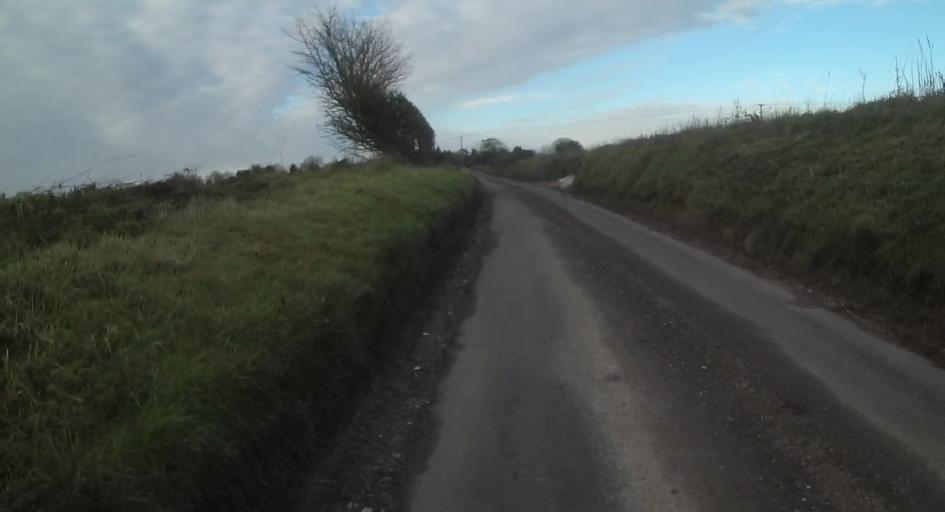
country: GB
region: England
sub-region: Hampshire
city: Basingstoke
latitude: 51.2791
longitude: -1.1547
